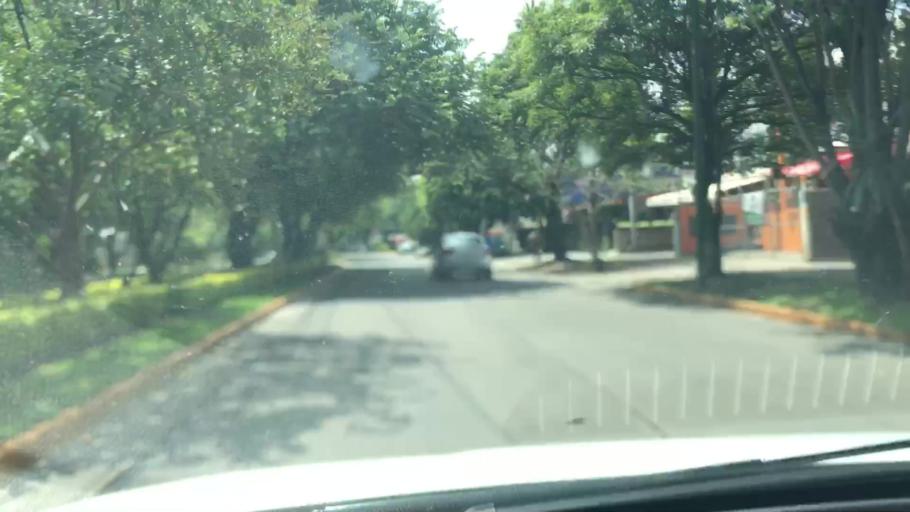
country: MX
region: Jalisco
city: Guadalajara
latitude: 20.6621
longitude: -103.4005
